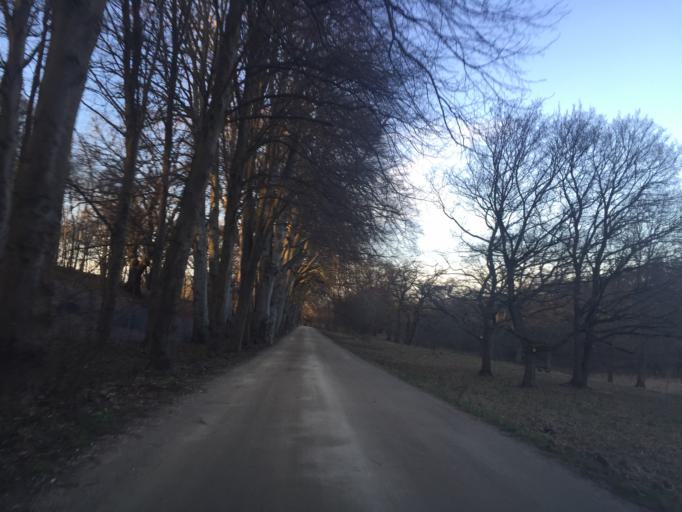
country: DK
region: Capital Region
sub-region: Lyngby-Tarbaek Kommune
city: Kongens Lyngby
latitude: 55.7874
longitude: 12.4971
